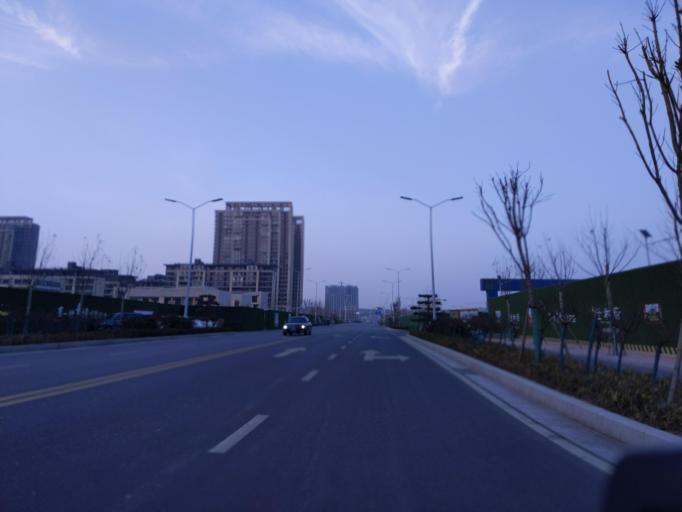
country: CN
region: Henan Sheng
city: Puyang
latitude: 35.8058
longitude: 115.0112
